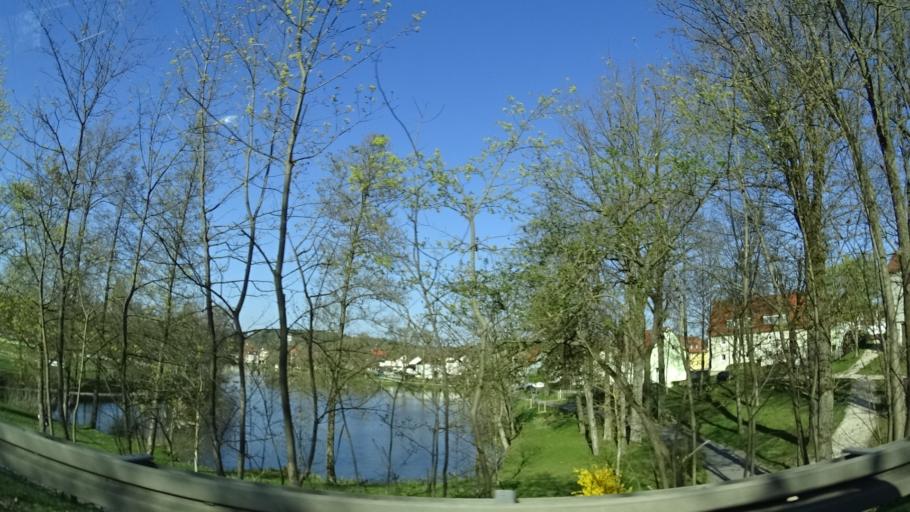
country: DE
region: Bavaria
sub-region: Upper Palatinate
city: Auerbach
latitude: 49.6929
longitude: 11.6214
